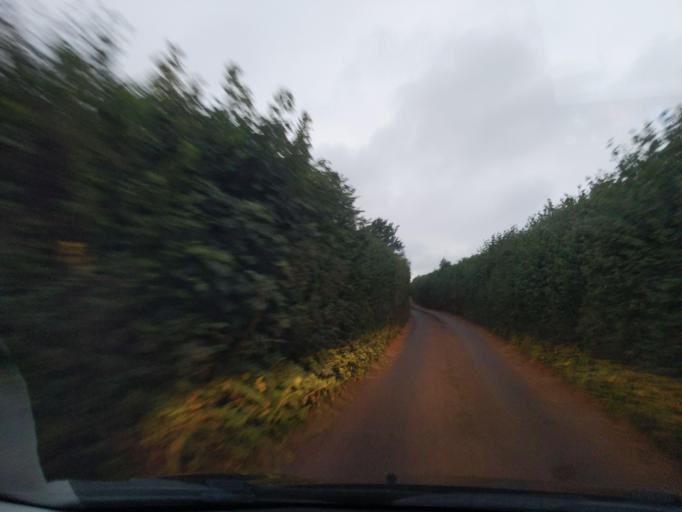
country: GB
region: England
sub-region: Devon
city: Marldon
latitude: 50.4621
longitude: -3.6062
